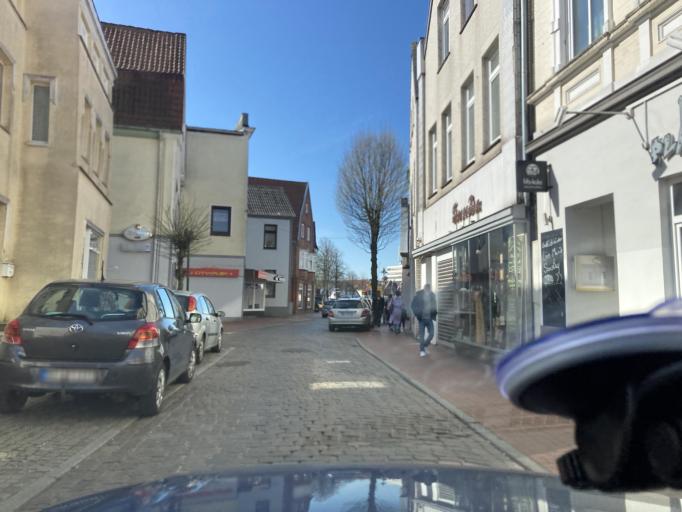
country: DE
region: Schleswig-Holstein
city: Heide
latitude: 54.1967
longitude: 9.0950
